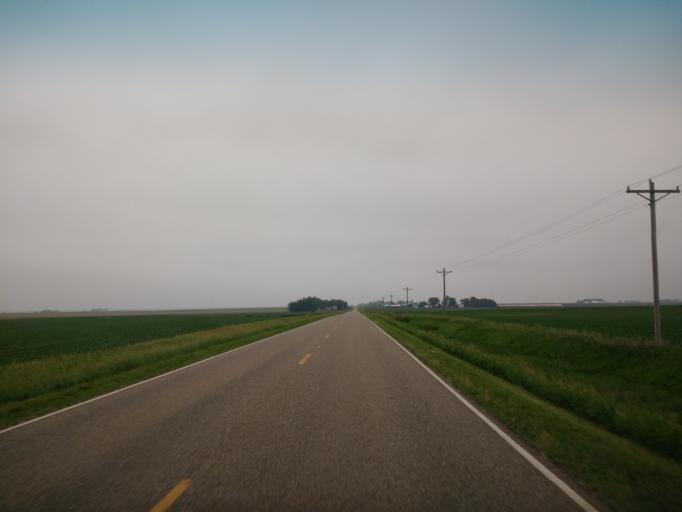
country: US
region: Iowa
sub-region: Sioux County
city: Alton
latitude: 43.0162
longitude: -95.8995
